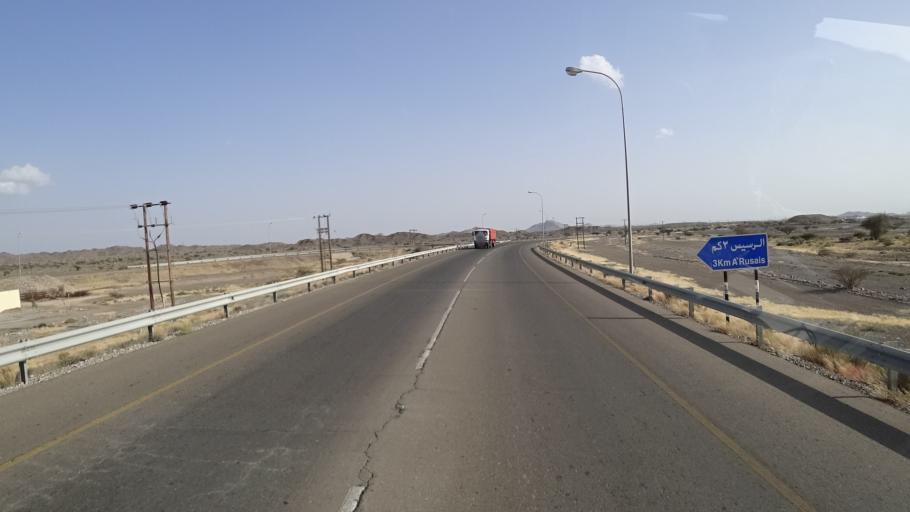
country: OM
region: Muhafazat ad Dakhiliyah
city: Izki
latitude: 22.8733
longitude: 57.7597
